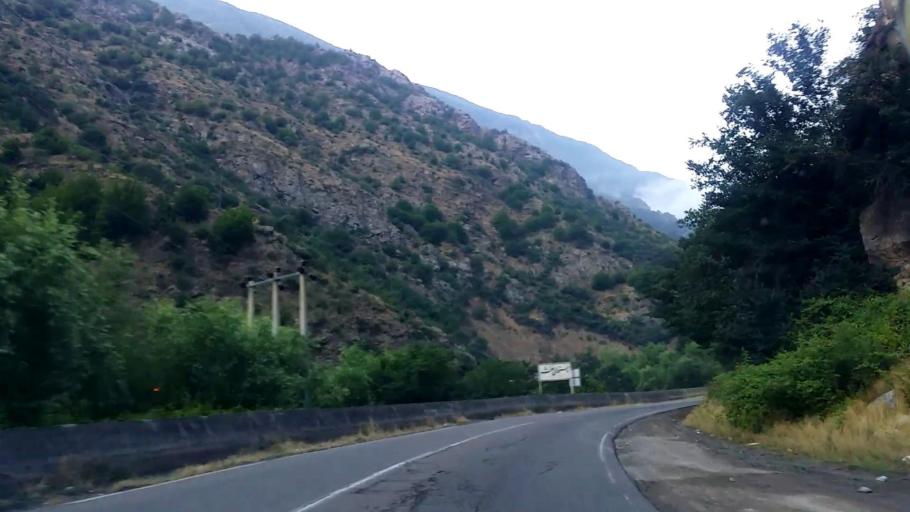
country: IR
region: Mazandaran
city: Chalus
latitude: 36.3069
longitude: 51.2475
